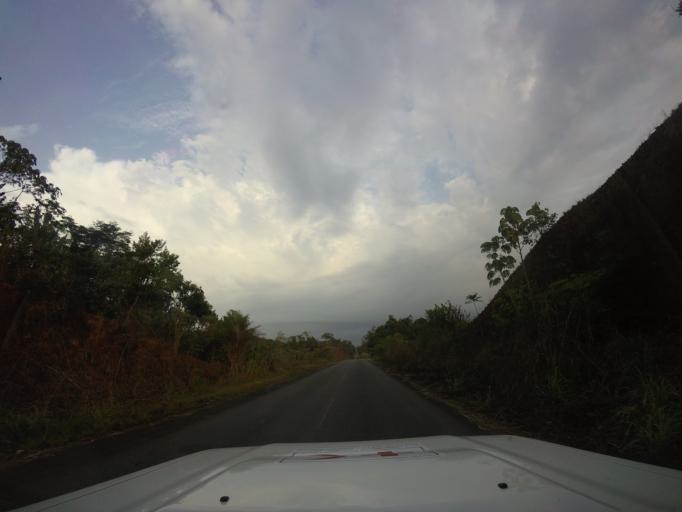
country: LR
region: Bomi
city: Tubmanburg
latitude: 6.6915
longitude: -10.8889
